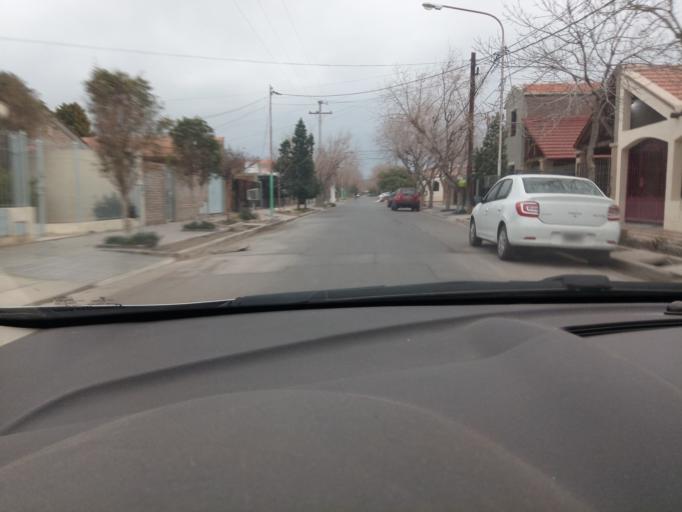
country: AR
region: San Juan
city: San Juan
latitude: -31.5350
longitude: -68.5954
